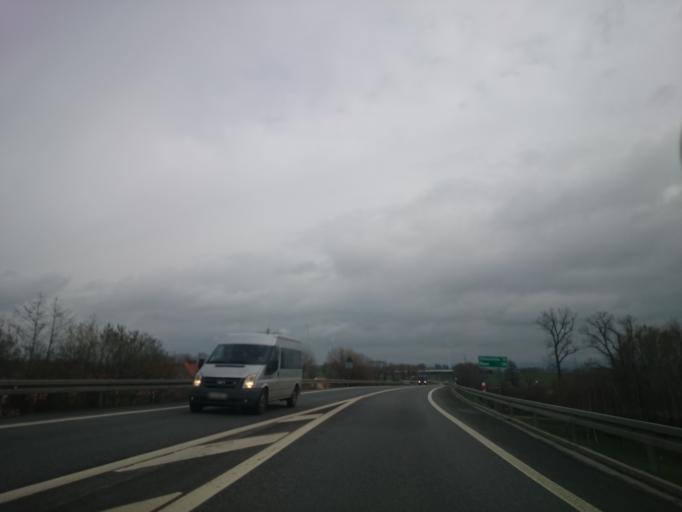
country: PL
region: Opole Voivodeship
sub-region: Powiat nyski
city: Paczkow
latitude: 50.4575
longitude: 16.9831
